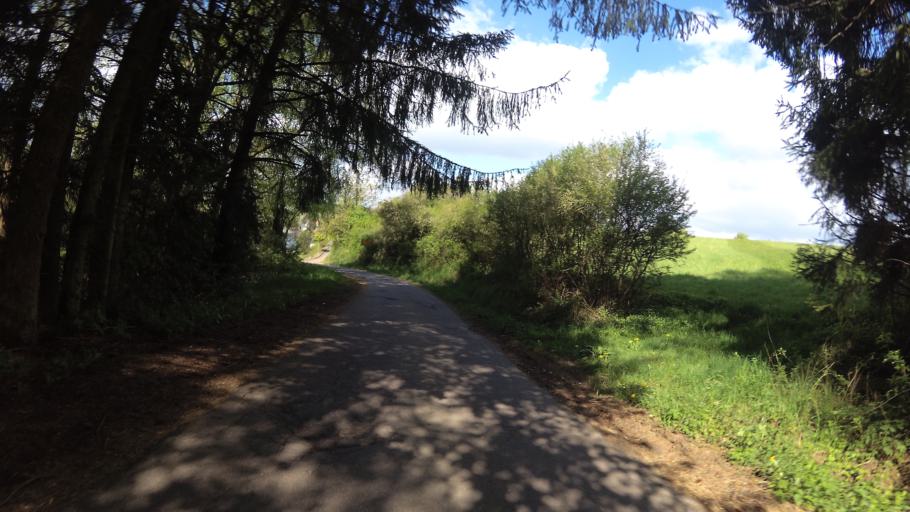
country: DE
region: Saarland
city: Lebach
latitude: 49.4835
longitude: 6.9484
